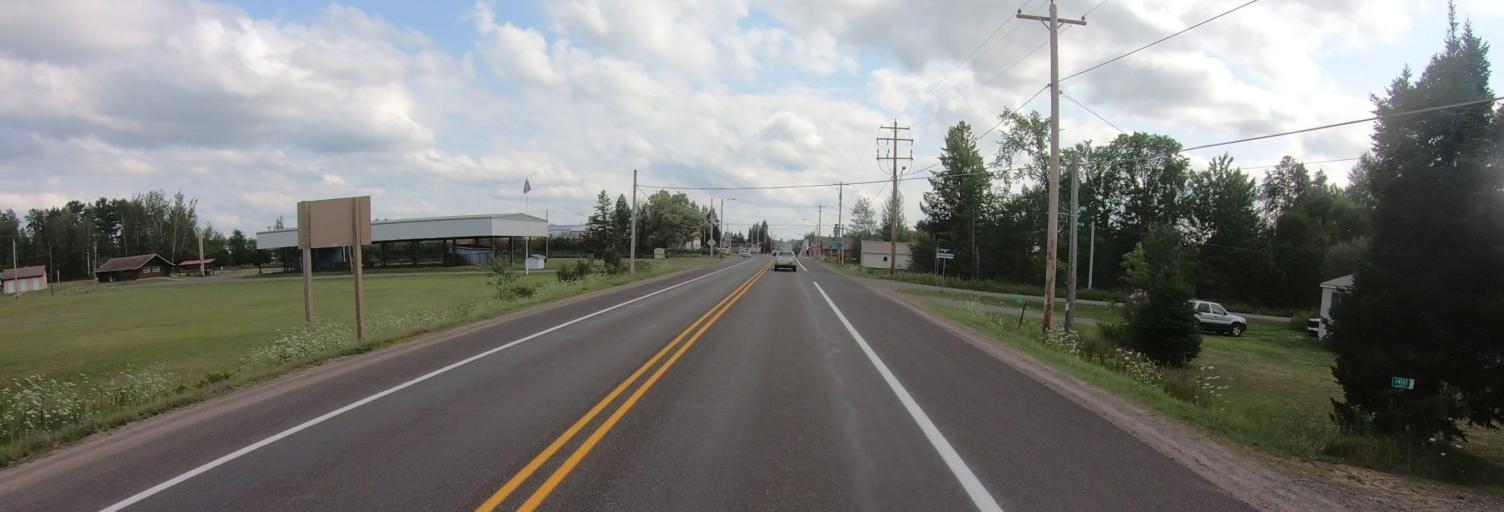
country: US
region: Michigan
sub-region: Ontonagon County
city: Ontonagon
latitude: 46.5375
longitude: -89.1785
